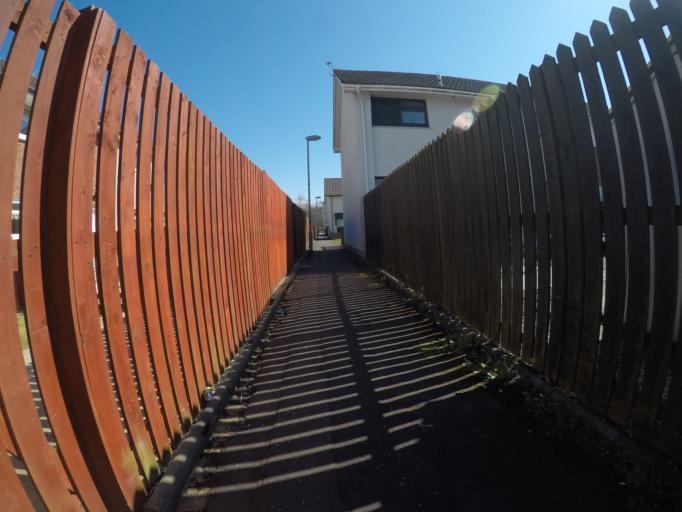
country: GB
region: Scotland
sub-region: North Ayrshire
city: Irvine
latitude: 55.6301
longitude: -4.6595
